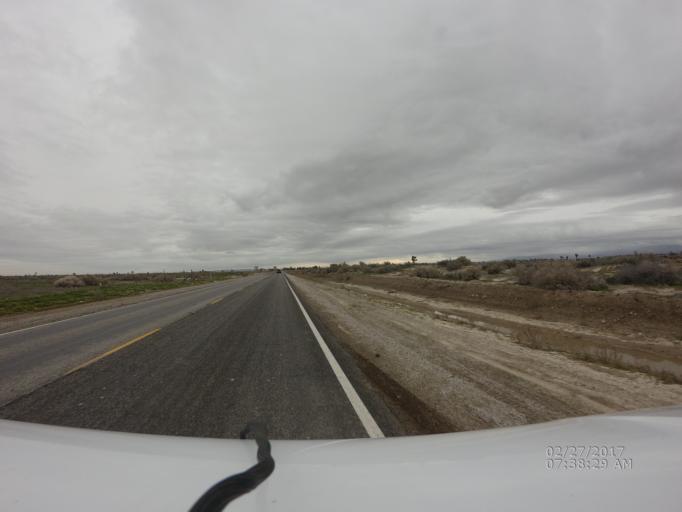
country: US
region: California
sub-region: Los Angeles County
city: Lancaster
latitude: 34.7189
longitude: -118.0870
